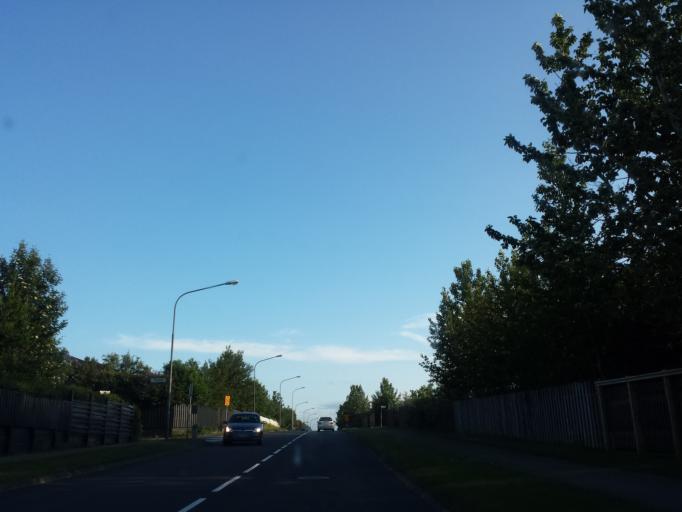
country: IS
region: Capital Region
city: Mosfellsbaer
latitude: 64.1112
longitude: -21.7860
